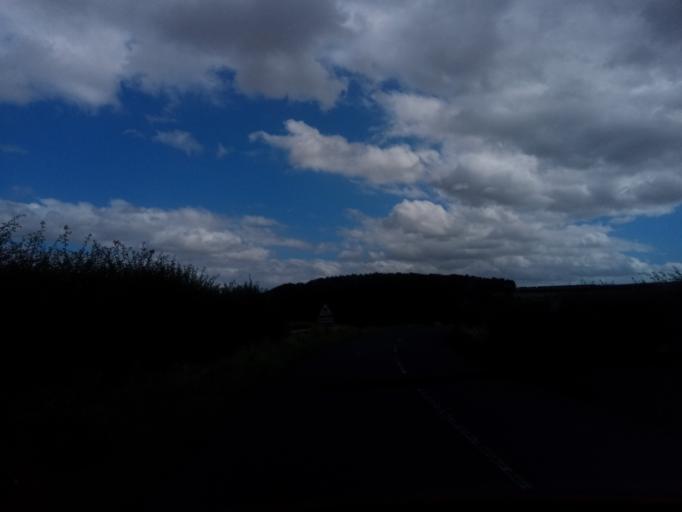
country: GB
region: Scotland
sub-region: The Scottish Borders
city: Coldstream
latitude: 55.6338
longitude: -2.3323
